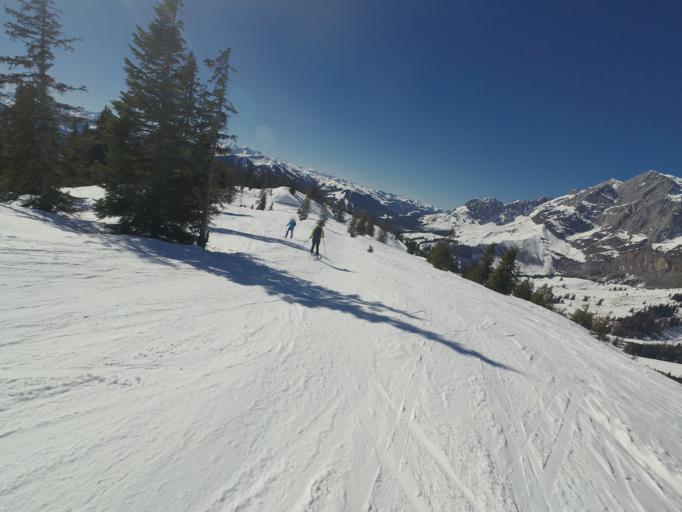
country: AT
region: Salzburg
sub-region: Politischer Bezirk Sankt Johann im Pongau
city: Muhlbach am Hochkonig
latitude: 47.4022
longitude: 13.1404
